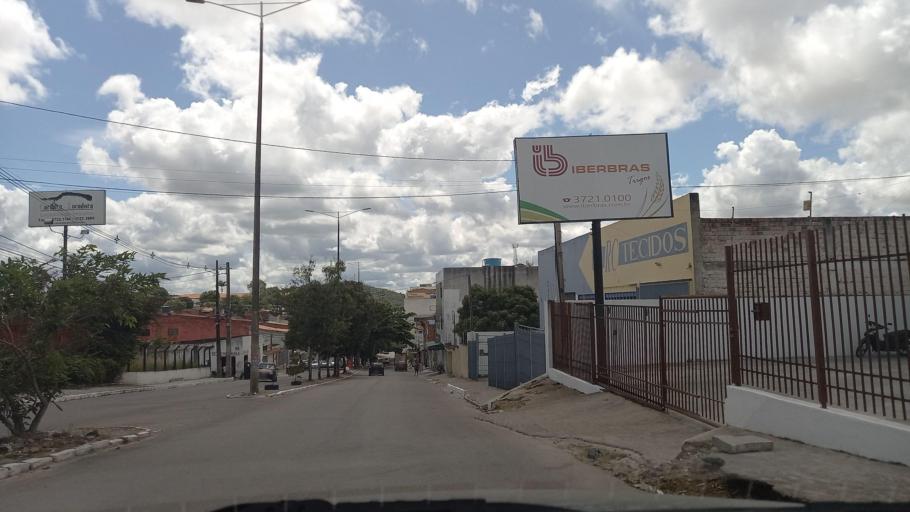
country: BR
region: Pernambuco
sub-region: Caruaru
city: Caruaru
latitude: -8.3020
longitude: -35.9730
